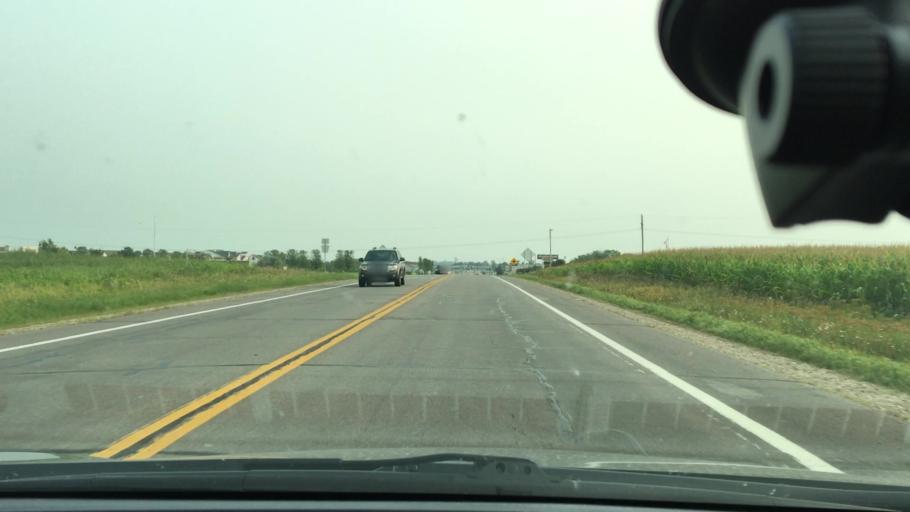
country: US
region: Minnesota
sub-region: Wright County
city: Albertville
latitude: 45.2510
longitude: -93.6633
